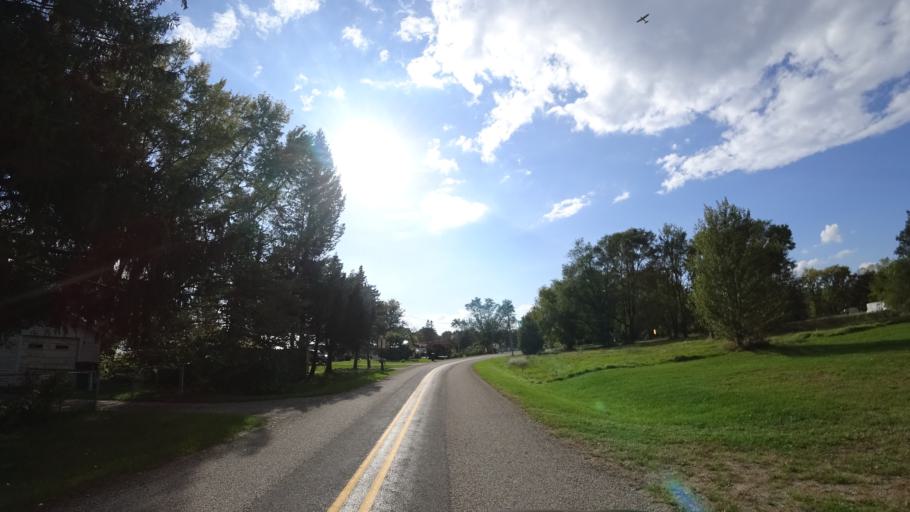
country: US
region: Michigan
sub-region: Saint Joseph County
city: Three Rivers
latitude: 41.9425
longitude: -85.6032
